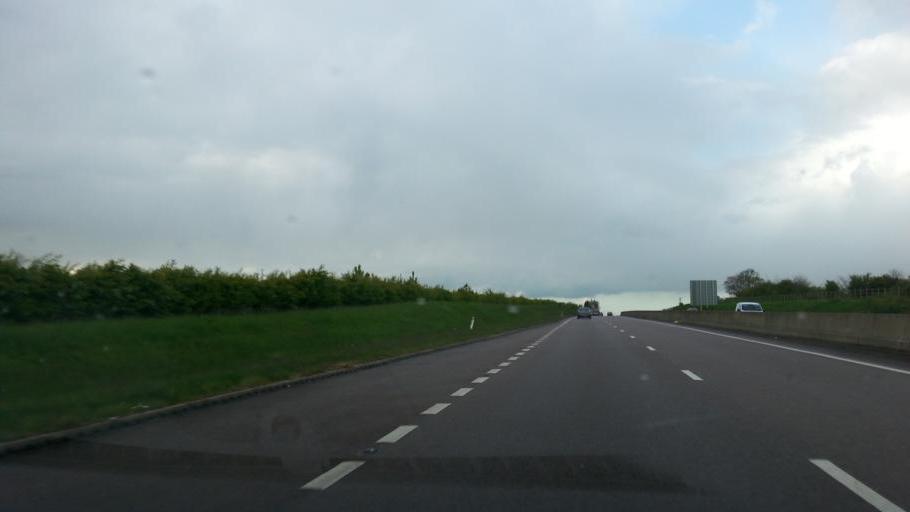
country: GB
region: England
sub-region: Nottinghamshire
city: East Bridgford
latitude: 52.9880
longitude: -0.9348
